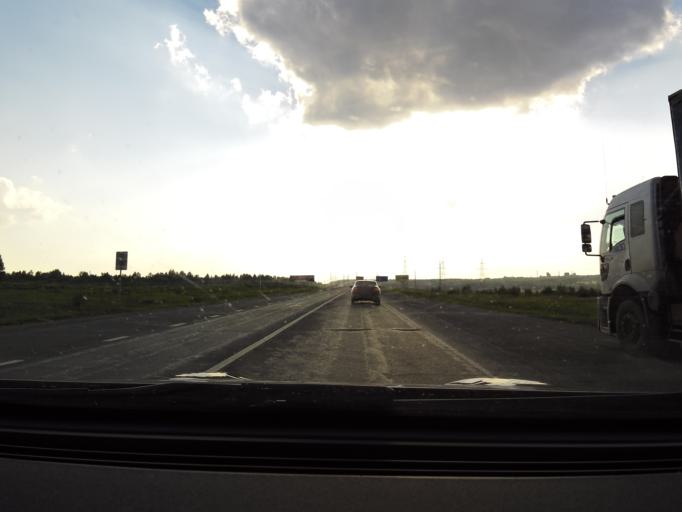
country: RU
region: Sverdlovsk
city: Revda
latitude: 56.8274
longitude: 59.9546
